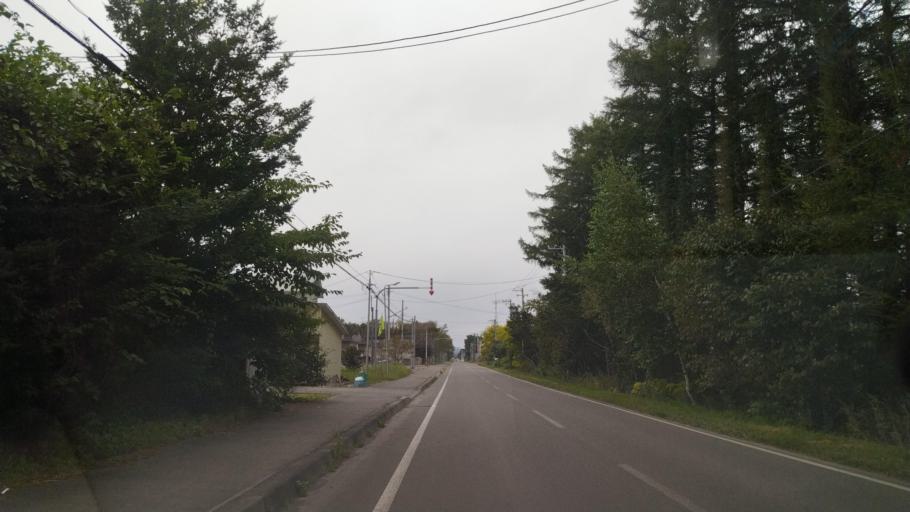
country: JP
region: Hokkaido
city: Otofuke
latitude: 43.2236
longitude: 143.2791
